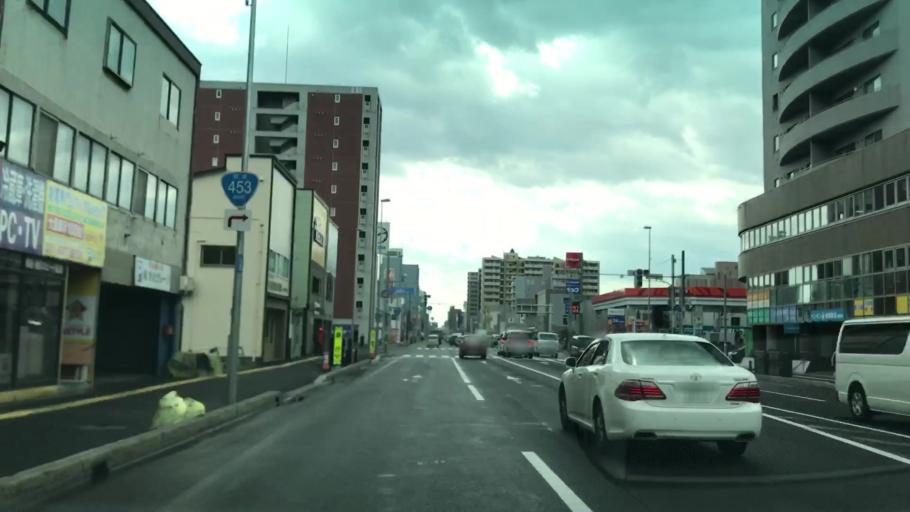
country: JP
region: Hokkaido
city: Sapporo
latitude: 43.0521
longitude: 141.3705
